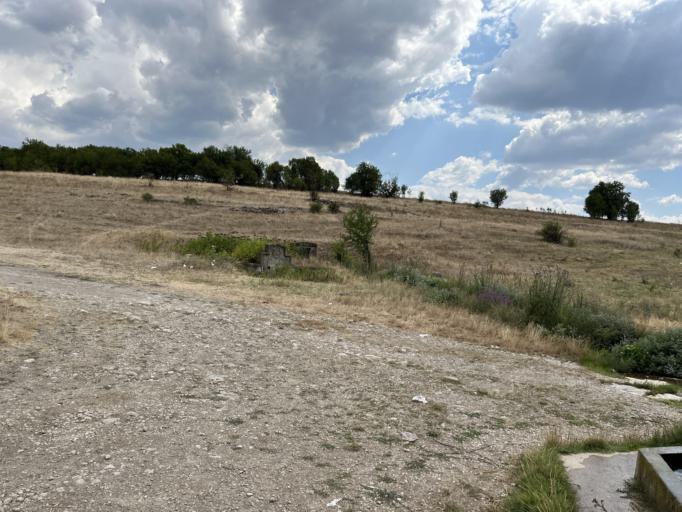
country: BG
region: Veliko Turnovo
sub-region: Obshtina Veliko Turnovo
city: Veliko Turnovo
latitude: 43.1375
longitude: 25.5063
